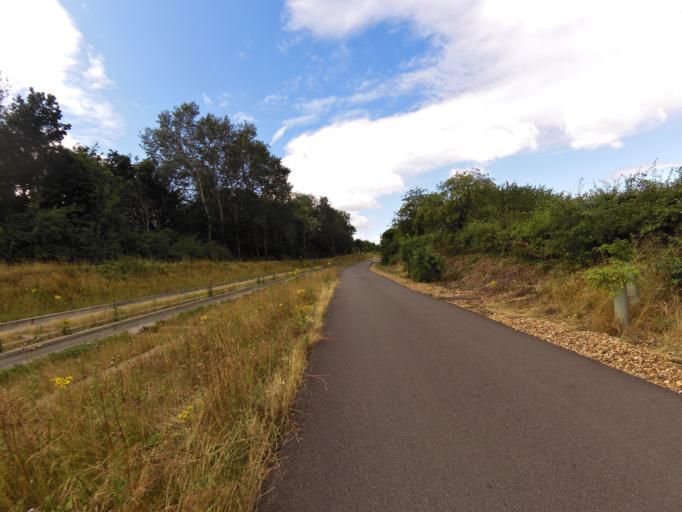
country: GB
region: England
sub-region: Cambridgeshire
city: Cambridge
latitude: 52.1716
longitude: 0.1211
